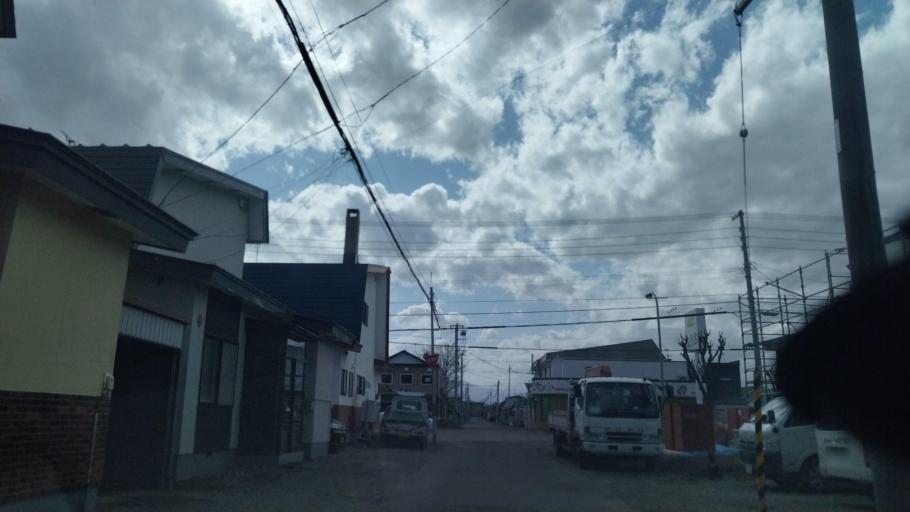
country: JP
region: Hokkaido
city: Obihiro
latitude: 42.9069
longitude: 143.1533
